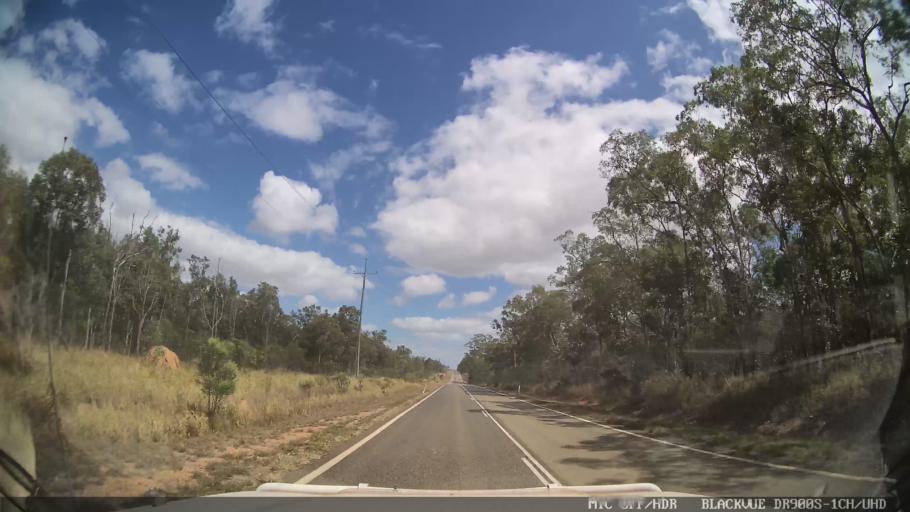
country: AU
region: Queensland
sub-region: Tablelands
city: Ravenshoe
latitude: -17.7224
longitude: 145.0525
